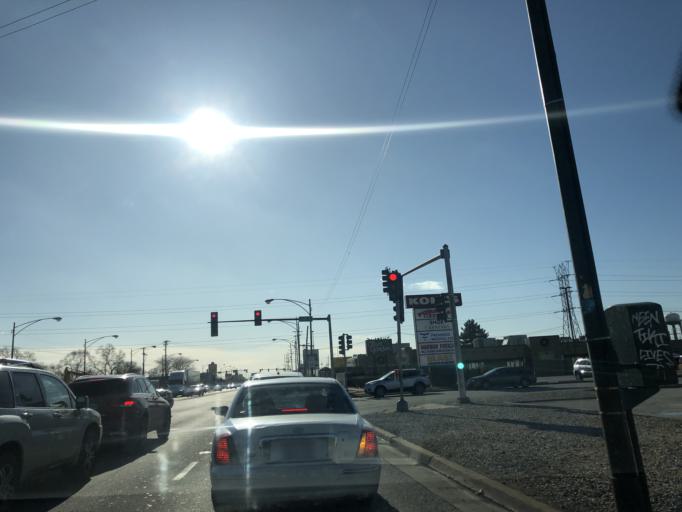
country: US
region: Illinois
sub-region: Cook County
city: Hometown
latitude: 41.7548
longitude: -87.7417
